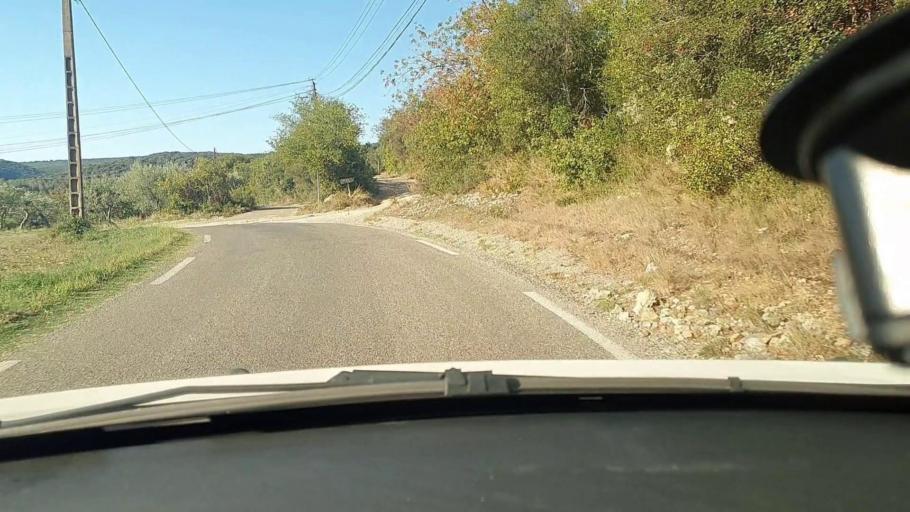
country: FR
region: Languedoc-Roussillon
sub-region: Departement du Gard
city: Goudargues
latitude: 44.2432
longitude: 4.4424
